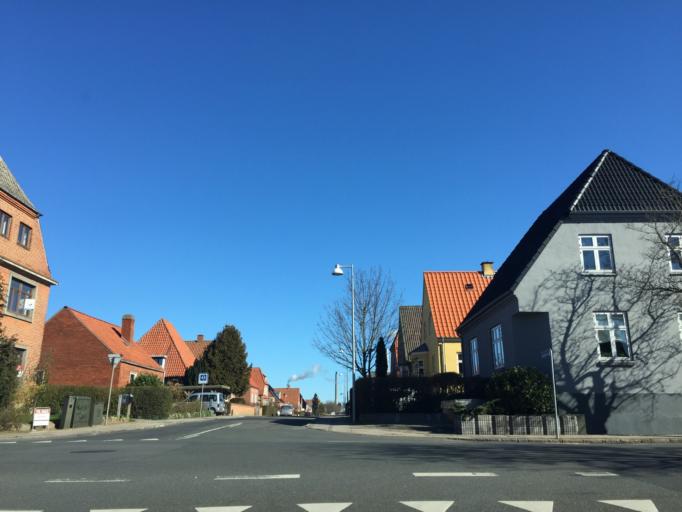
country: DK
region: South Denmark
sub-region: Odense Kommune
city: Odense
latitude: 55.4127
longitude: 10.3993
